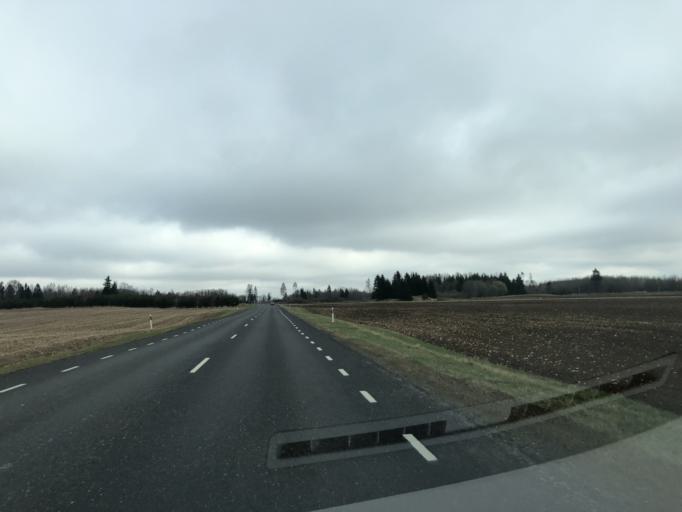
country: EE
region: Laeaene-Virumaa
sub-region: Rakvere linn
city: Rakvere
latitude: 59.2575
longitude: 26.2831
